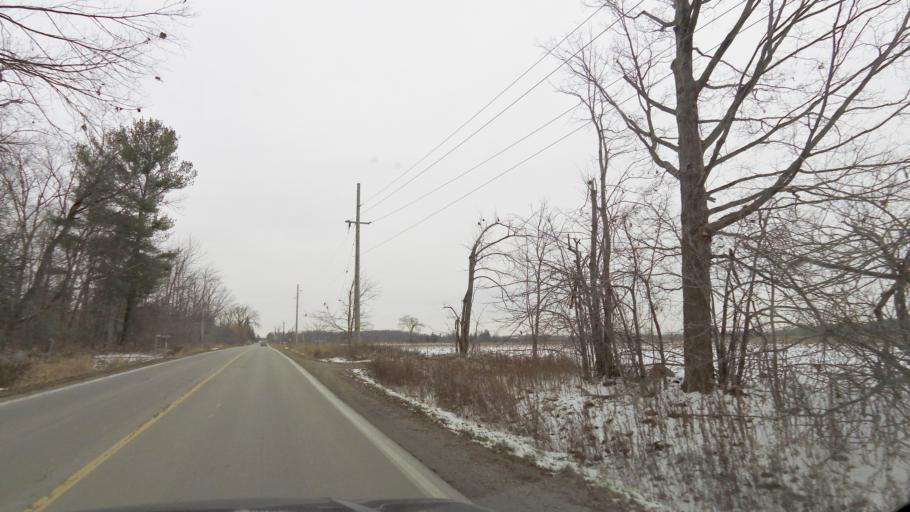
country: CA
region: Ontario
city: Vaughan
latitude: 43.8594
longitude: -79.5909
